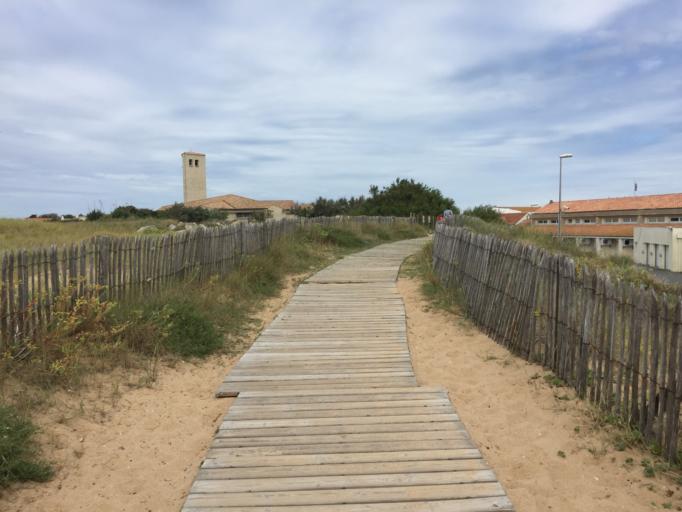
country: FR
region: Poitou-Charentes
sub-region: Departement de la Charente-Maritime
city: Dolus-d'Oleron
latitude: 45.9141
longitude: -1.3300
